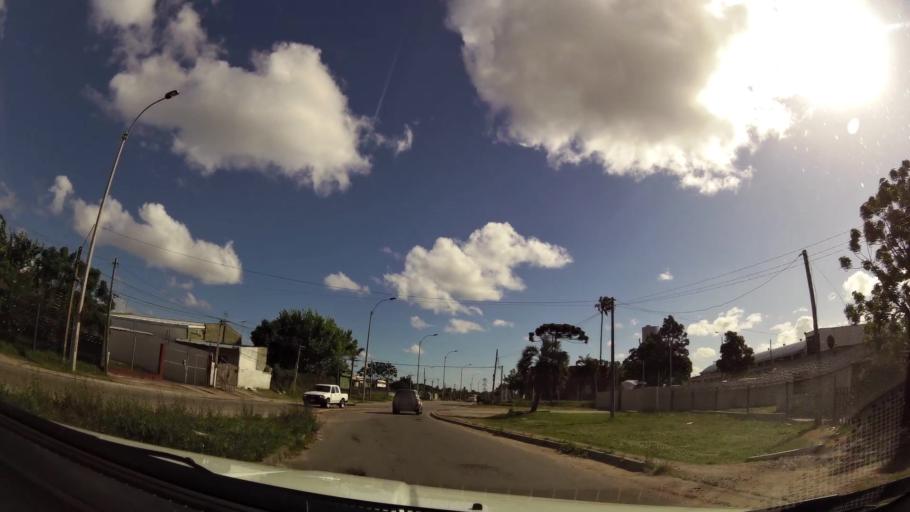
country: UY
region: Canelones
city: La Paz
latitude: -34.8164
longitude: -56.2333
